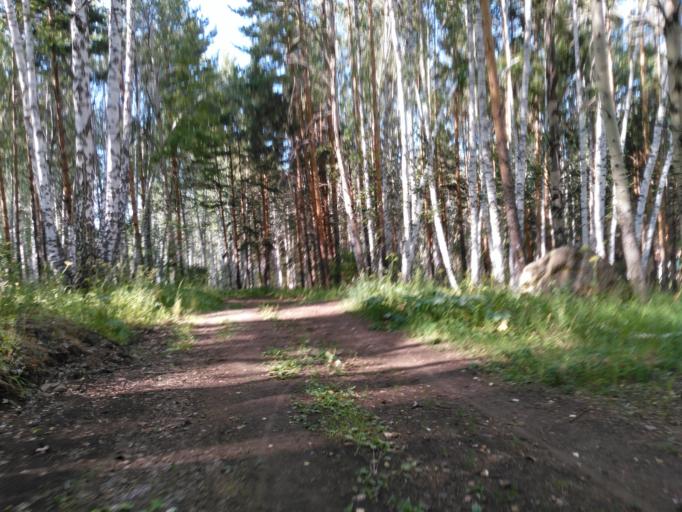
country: RU
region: Bashkortostan
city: Uchaly
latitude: 54.3317
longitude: 59.3577
